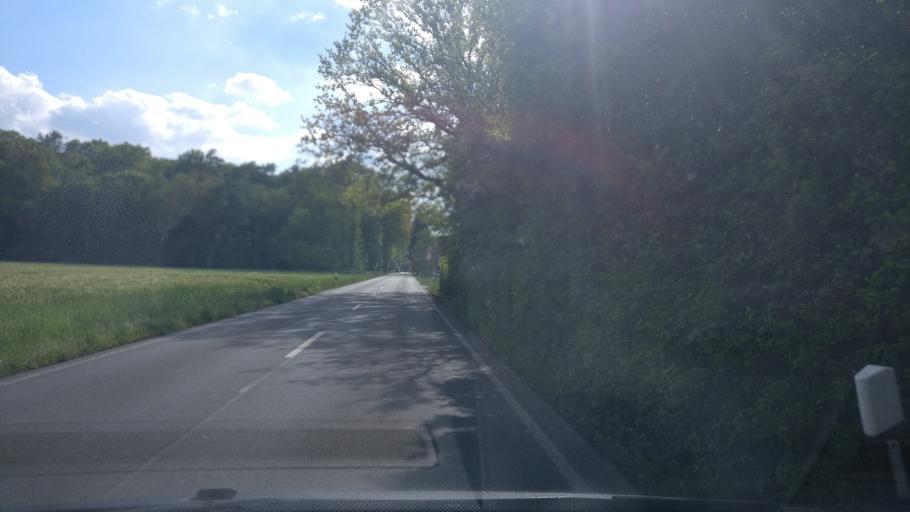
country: DE
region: North Rhine-Westphalia
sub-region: Regierungsbezirk Detmold
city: Leopoldshohe
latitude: 52.0034
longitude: 8.7362
